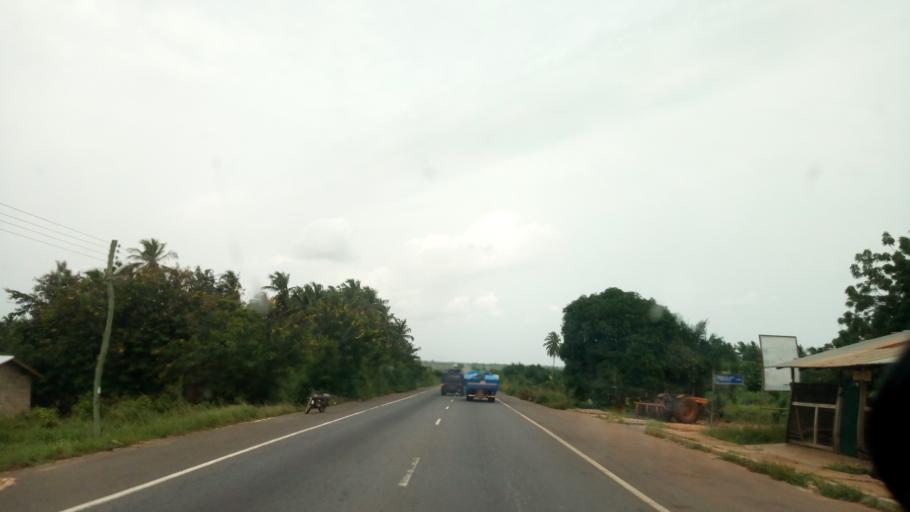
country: GH
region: Volta
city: Keta
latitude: 6.0640
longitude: 0.9198
